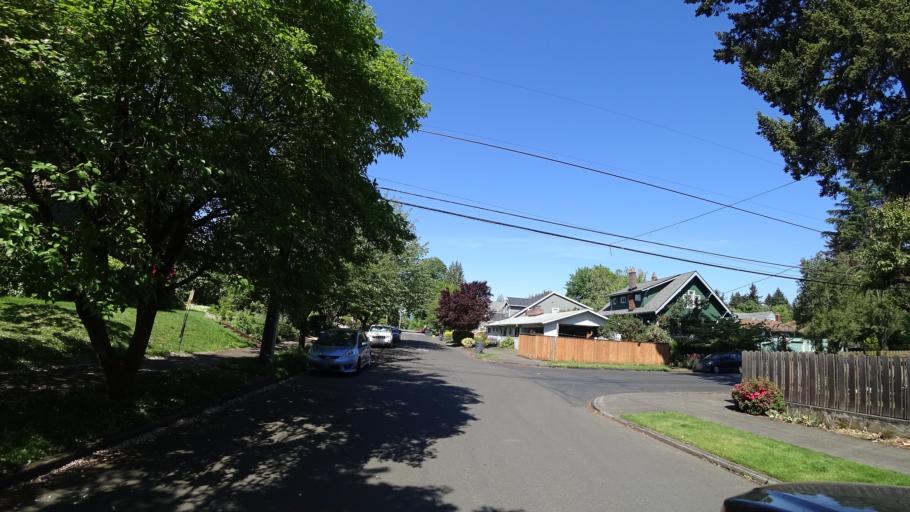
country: US
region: Oregon
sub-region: Multnomah County
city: Lents
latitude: 45.4935
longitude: -122.6139
